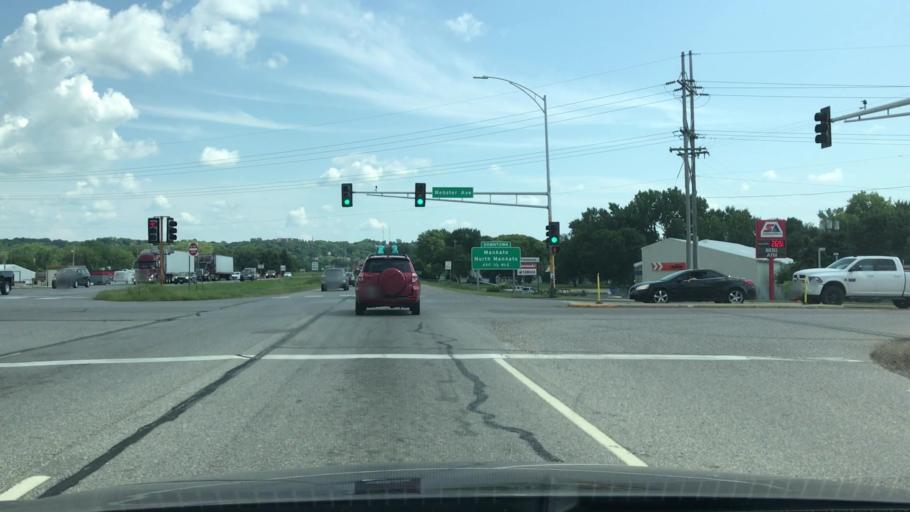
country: US
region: Minnesota
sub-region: Blue Earth County
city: Mankato
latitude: 44.1816
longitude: -94.0081
